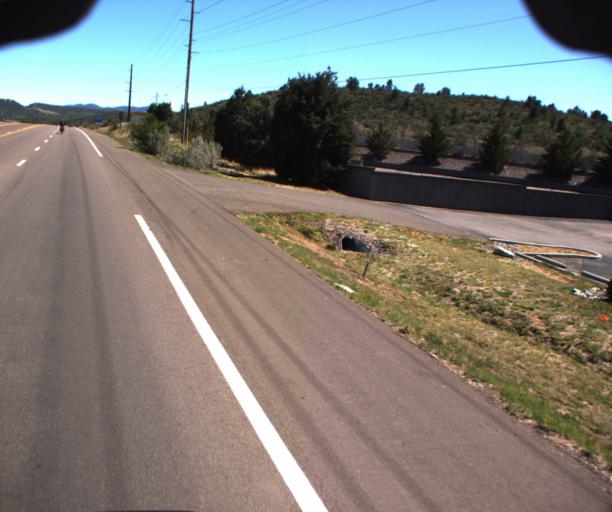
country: US
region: Arizona
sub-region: Yavapai County
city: Prescott
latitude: 34.5916
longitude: -112.4256
